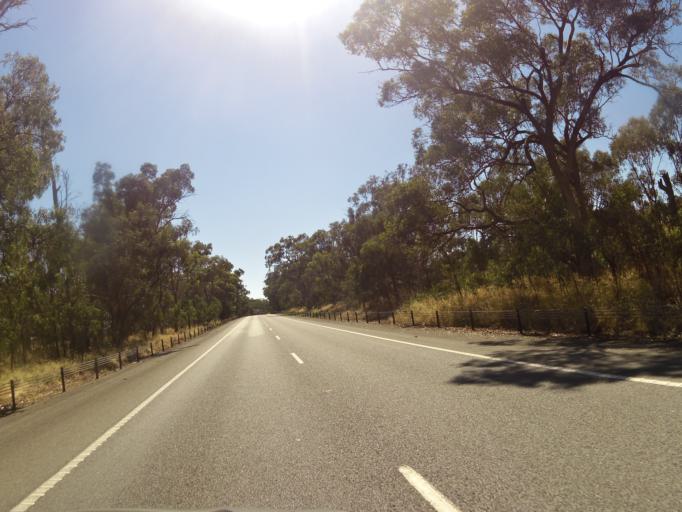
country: AU
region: Victoria
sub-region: Greater Shepparton
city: Shepparton
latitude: -36.7726
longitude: 145.5181
